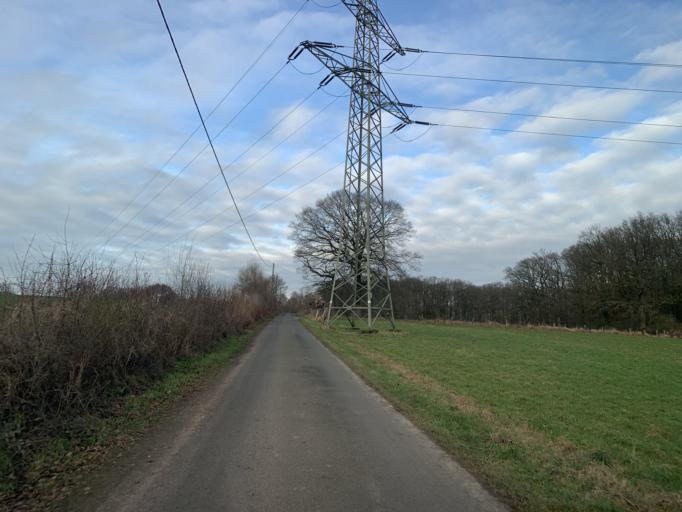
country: DE
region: North Rhine-Westphalia
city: Ludinghausen
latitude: 51.7733
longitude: 7.4046
